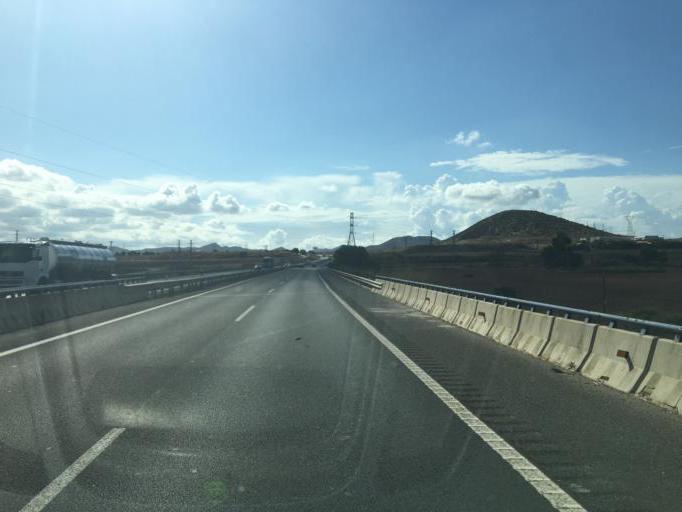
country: ES
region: Murcia
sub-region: Murcia
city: Cartagena
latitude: 37.6393
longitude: -0.9609
